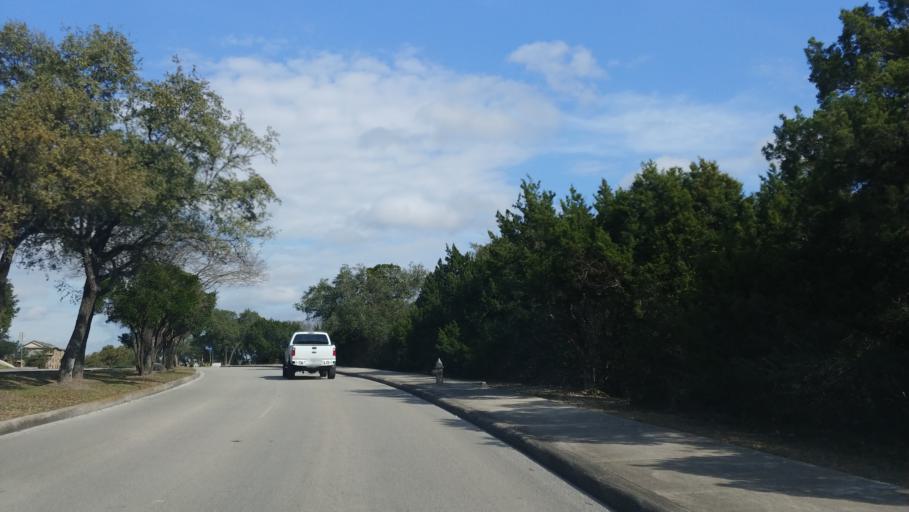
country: US
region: Texas
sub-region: Bexar County
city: Cross Mountain
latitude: 29.6188
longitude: -98.6113
